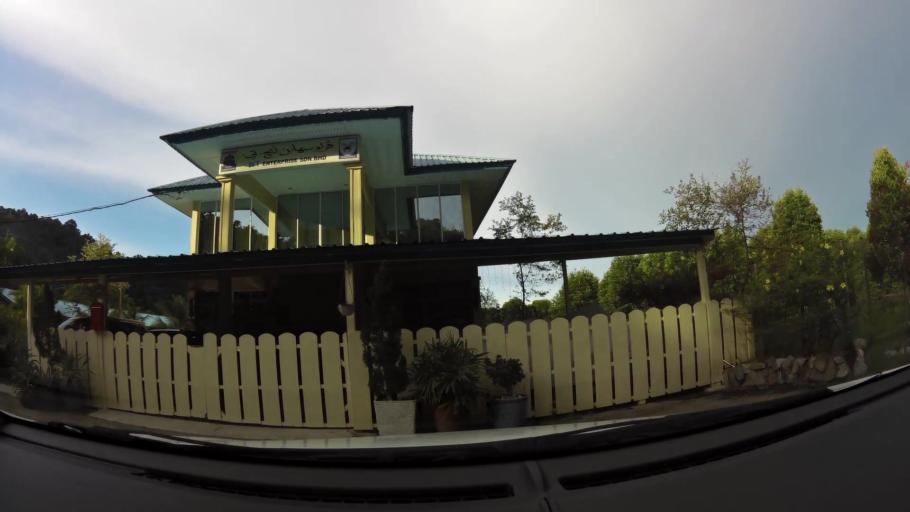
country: BN
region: Brunei and Muara
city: Bandar Seri Begawan
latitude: 4.9120
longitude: 115.0040
